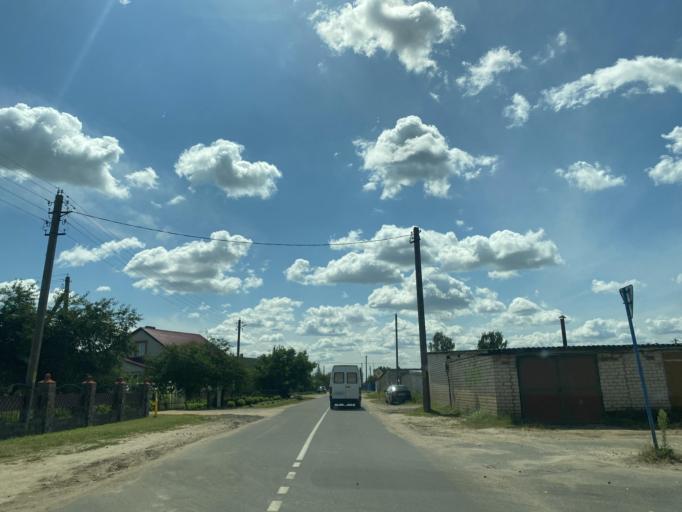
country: BY
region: Brest
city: Ivanava
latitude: 52.1448
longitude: 25.5466
